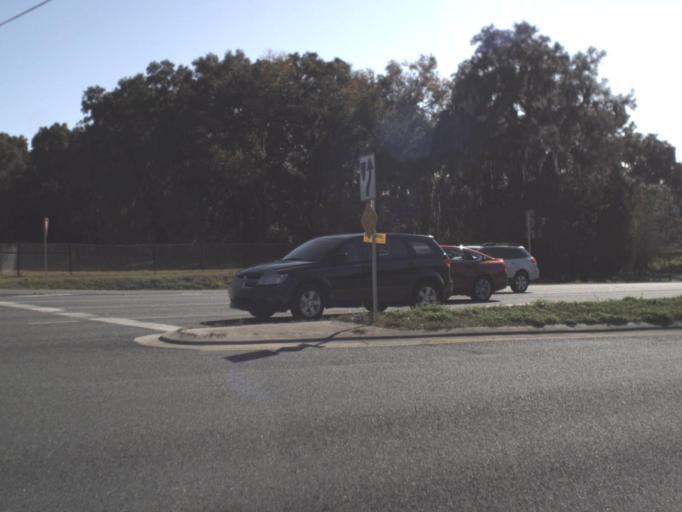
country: US
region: Florida
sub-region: Marion County
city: Belleview
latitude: 29.0291
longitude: -82.0451
